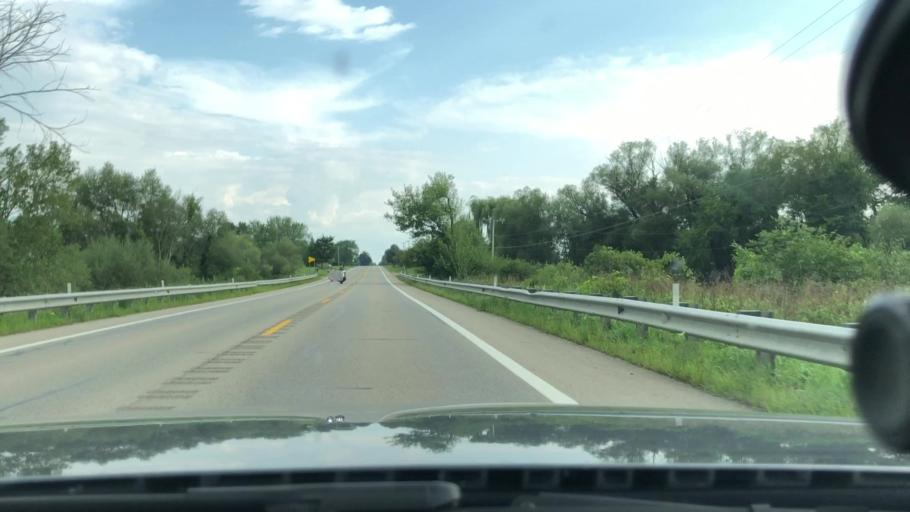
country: US
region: Michigan
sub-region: Washtenaw County
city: Manchester
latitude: 42.2138
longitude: -84.0332
